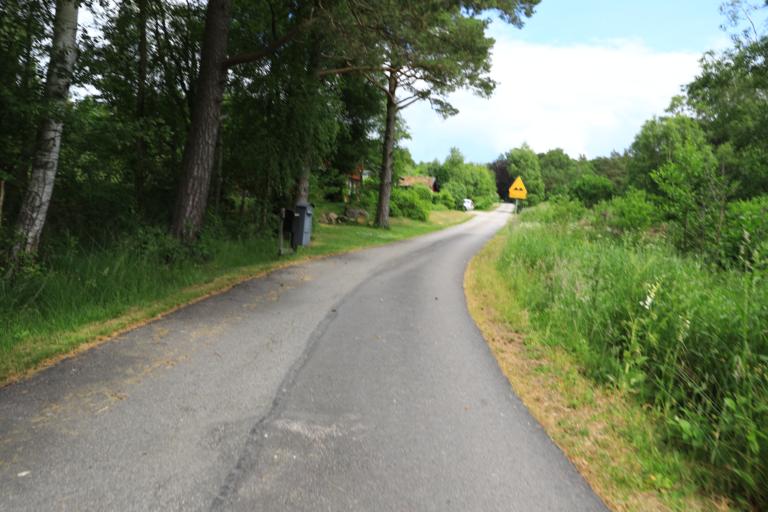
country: SE
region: Halland
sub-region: Varbergs Kommun
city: Varberg
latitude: 57.1672
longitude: 12.2553
